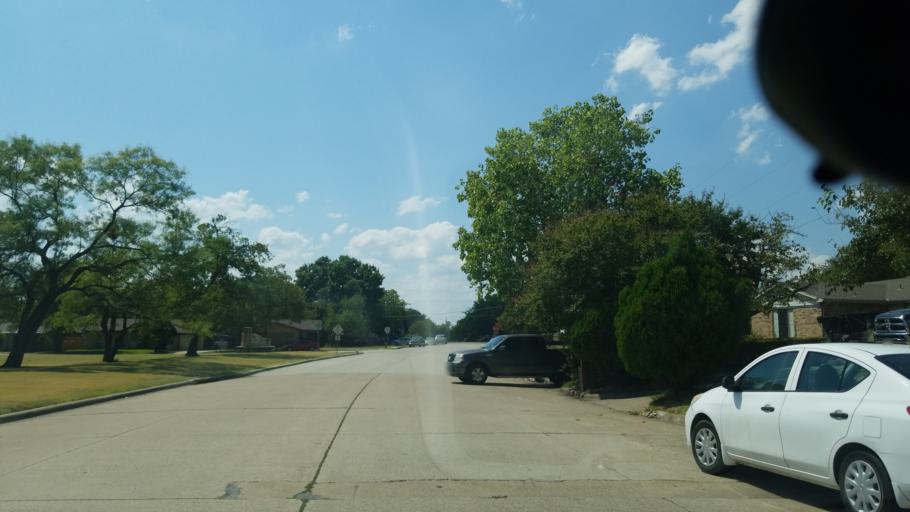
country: US
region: Texas
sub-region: Dallas County
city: Grand Prairie
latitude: 32.7112
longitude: -96.9810
